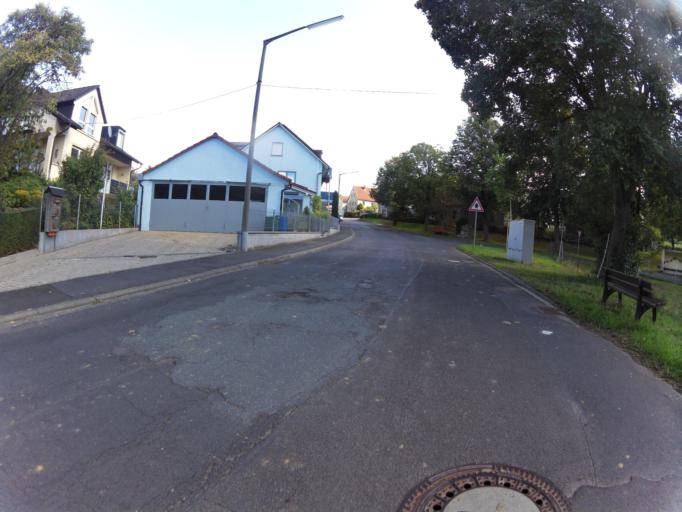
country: DE
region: Bavaria
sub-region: Regierungsbezirk Unterfranken
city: Frickenhausen
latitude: 49.6883
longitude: 10.0819
